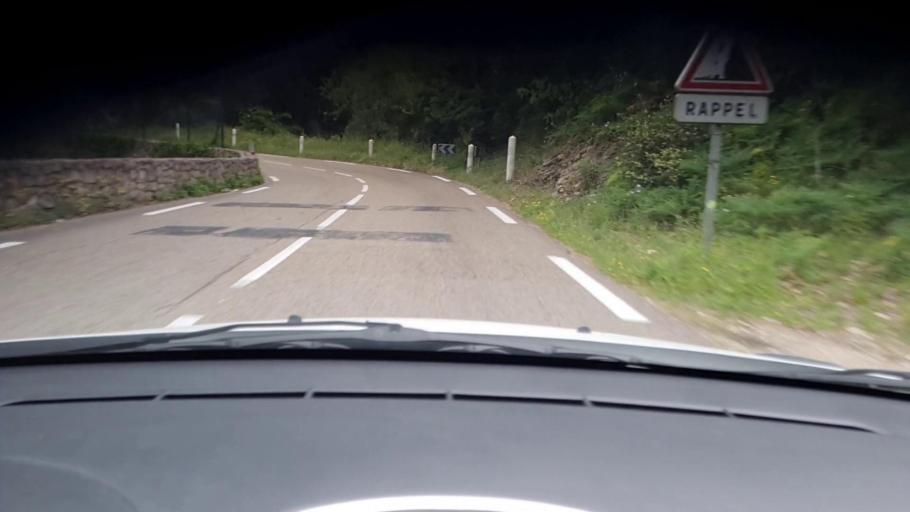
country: FR
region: Languedoc-Roussillon
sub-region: Departement du Gard
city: Blauzac
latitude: 43.9400
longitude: 4.3818
